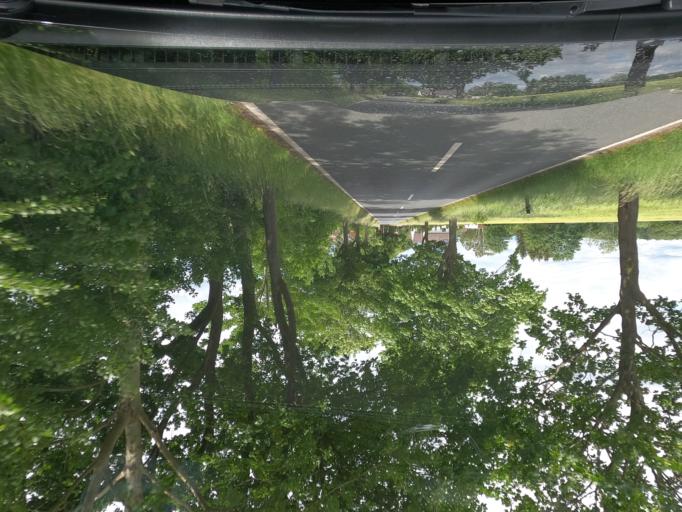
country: DE
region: Lower Saxony
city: Lehrte
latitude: 52.4107
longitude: 9.9375
